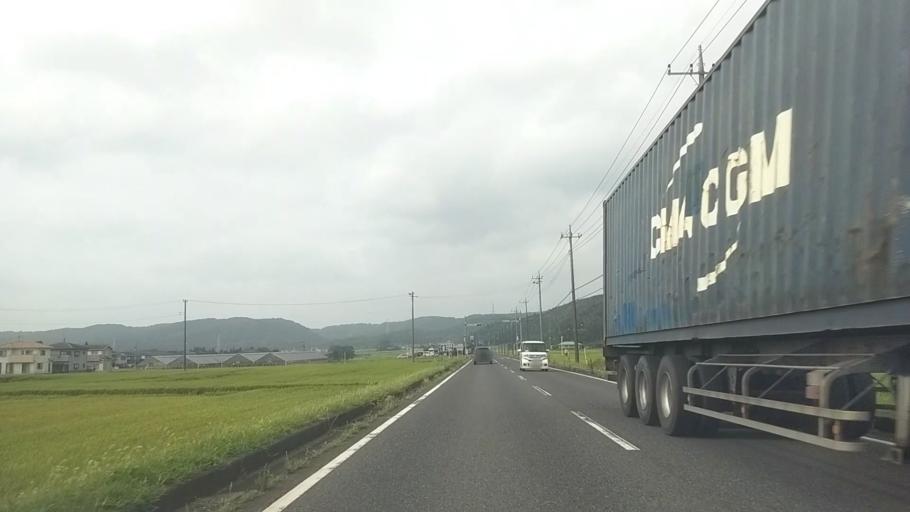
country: JP
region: Chiba
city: Kimitsu
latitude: 35.2884
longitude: 139.9903
